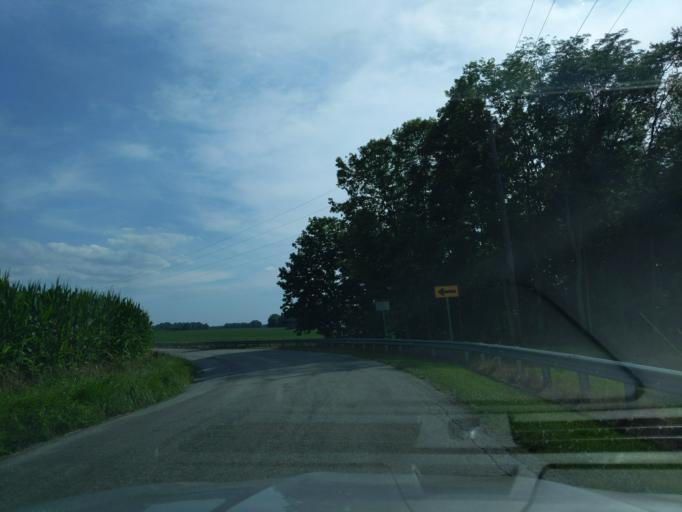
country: US
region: Indiana
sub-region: Decatur County
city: Greensburg
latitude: 39.2572
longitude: -85.4696
